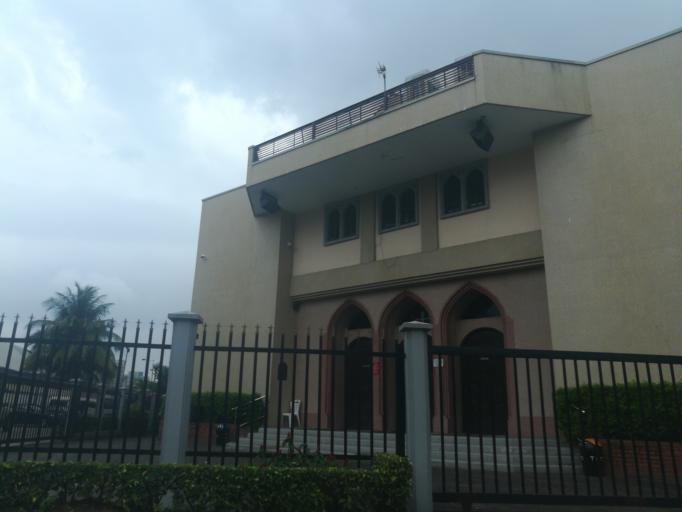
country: NG
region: Lagos
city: Lagos
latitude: 6.4465
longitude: 3.3991
